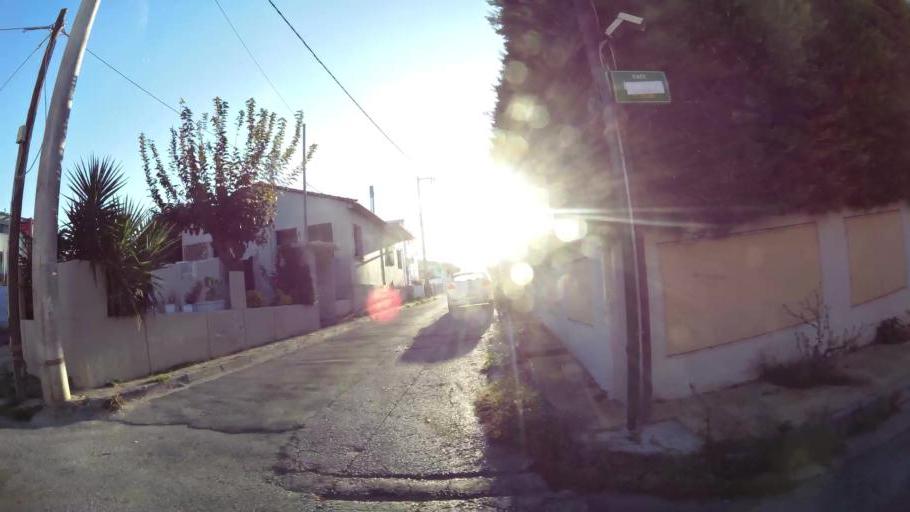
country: GR
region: Attica
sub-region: Nomarchia Anatolikis Attikis
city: Gerakas
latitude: 38.0331
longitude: 23.8553
